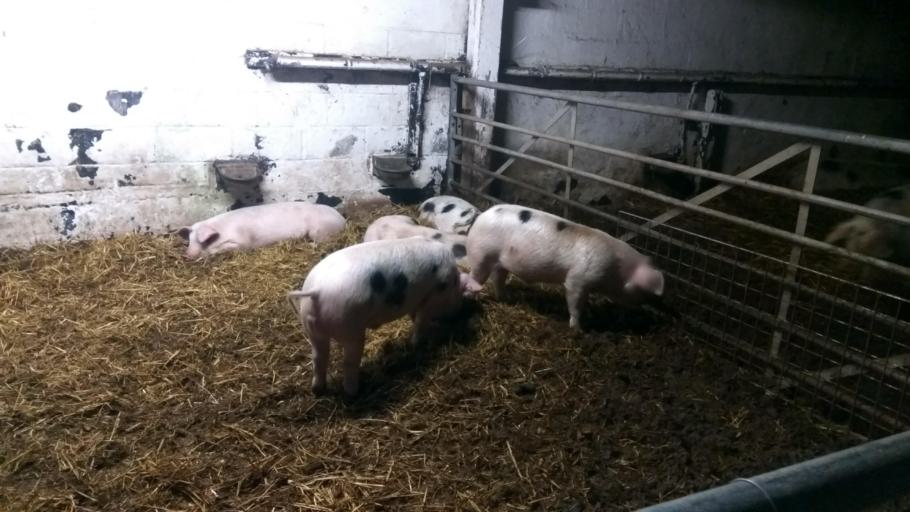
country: GB
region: England
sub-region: City and Borough of Leeds
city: Chapel Allerton
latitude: 53.8187
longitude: -1.5516
